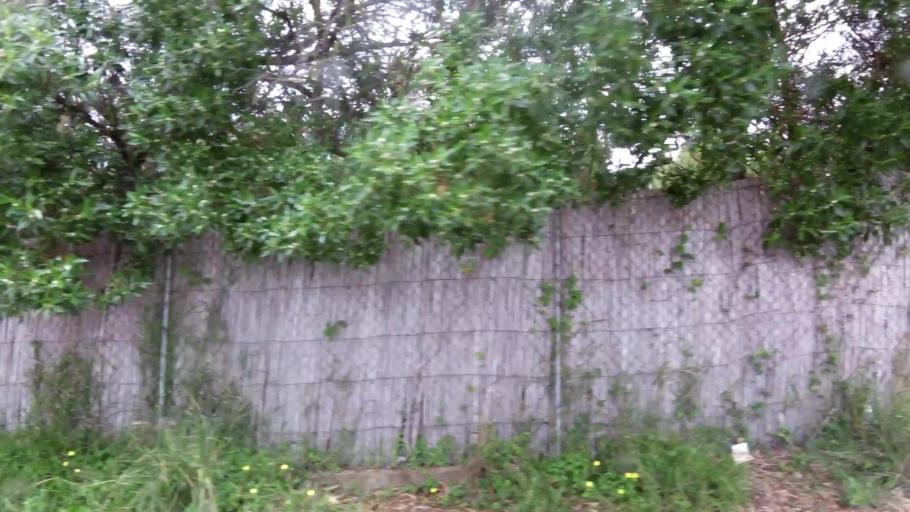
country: MA
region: Tanger-Tetouan
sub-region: Tanger-Assilah
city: Tangier
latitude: 35.7799
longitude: -5.8584
